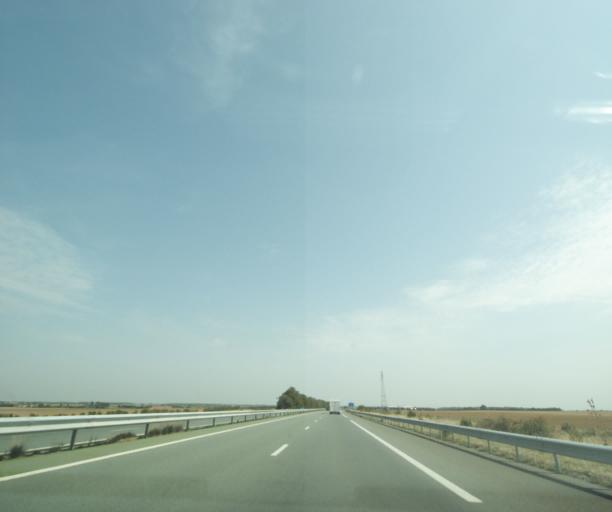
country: FR
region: Poitou-Charentes
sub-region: Departement des Deux-Sevres
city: Villiers-en-Plaine
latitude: 46.4291
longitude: -0.5194
